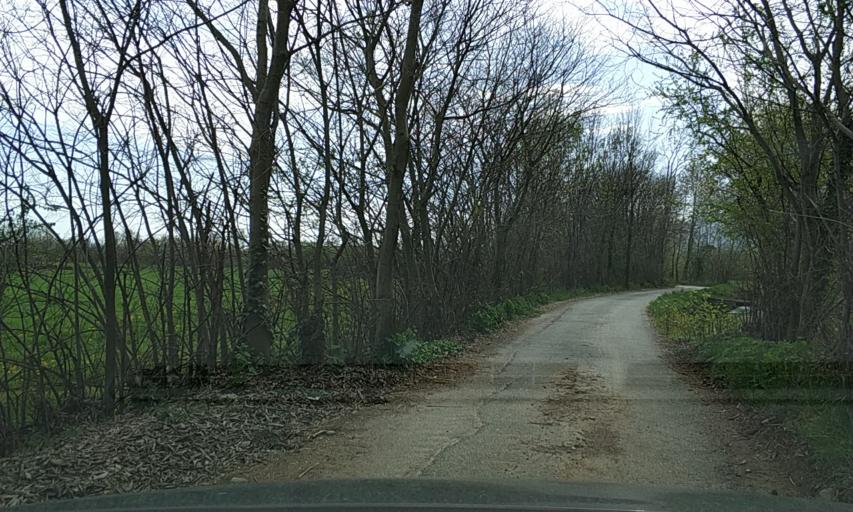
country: IT
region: Piedmont
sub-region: Provincia di Torino
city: Nole
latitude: 45.2320
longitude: 7.5731
